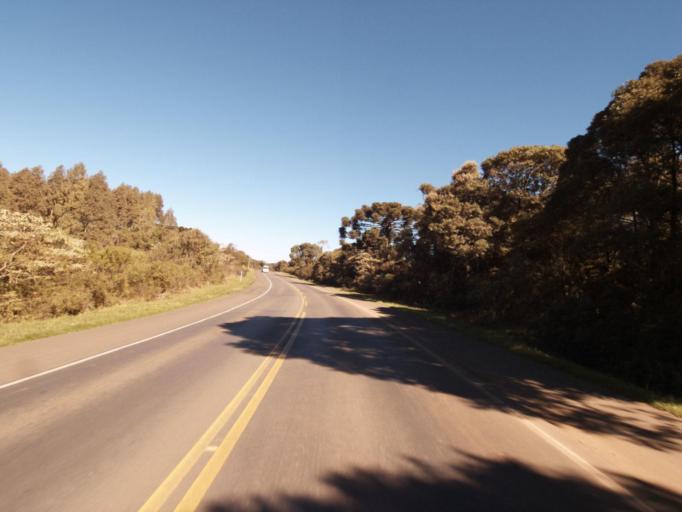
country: BR
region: Santa Catarina
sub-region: Xanxere
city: Xanxere
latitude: -26.8775
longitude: -52.1601
